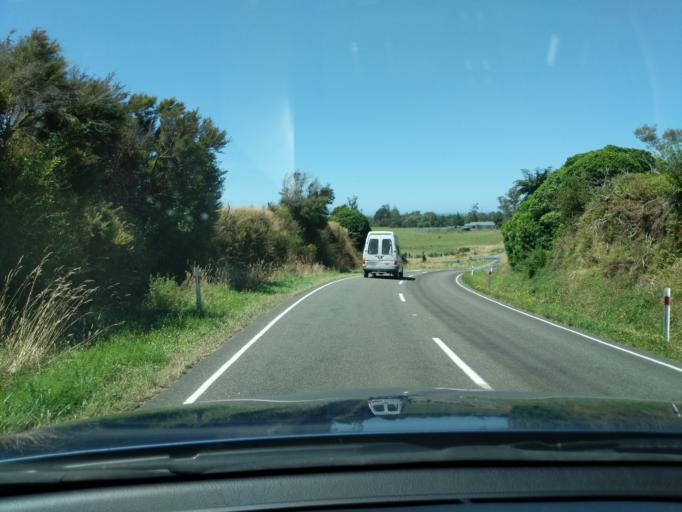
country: NZ
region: Tasman
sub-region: Tasman District
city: Takaka
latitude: -40.6876
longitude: 172.6485
